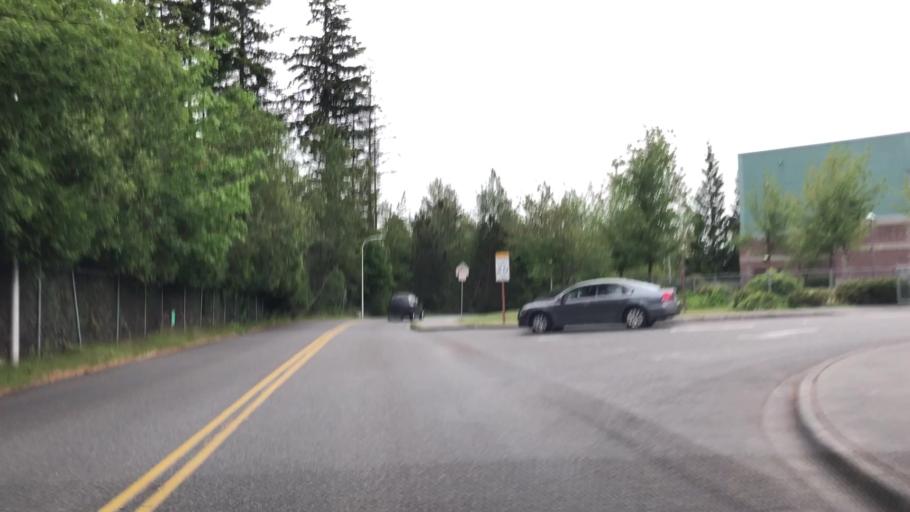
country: US
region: Washington
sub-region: Snohomish County
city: Mill Creek
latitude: 47.8745
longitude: -122.2093
